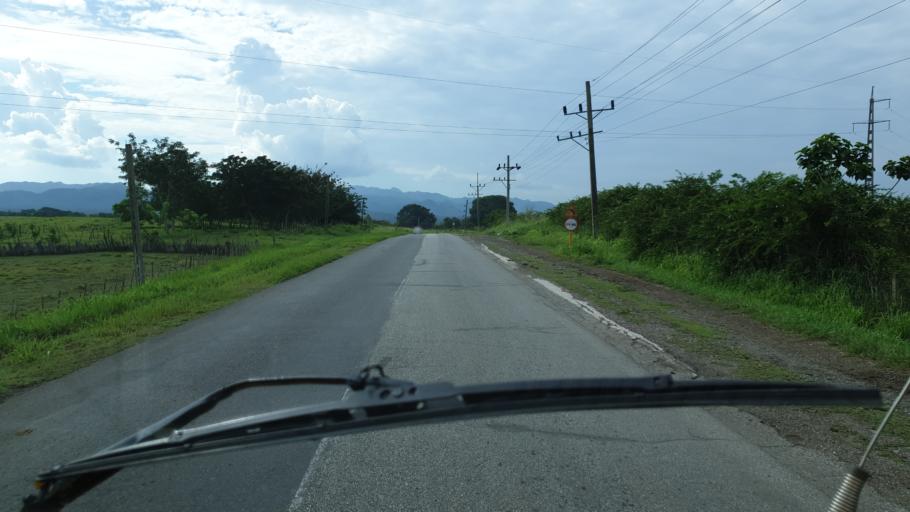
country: CU
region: Cienfuegos
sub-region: Municipio de Cienfuegos
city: Cumanayagua
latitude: 22.0722
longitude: -80.3071
